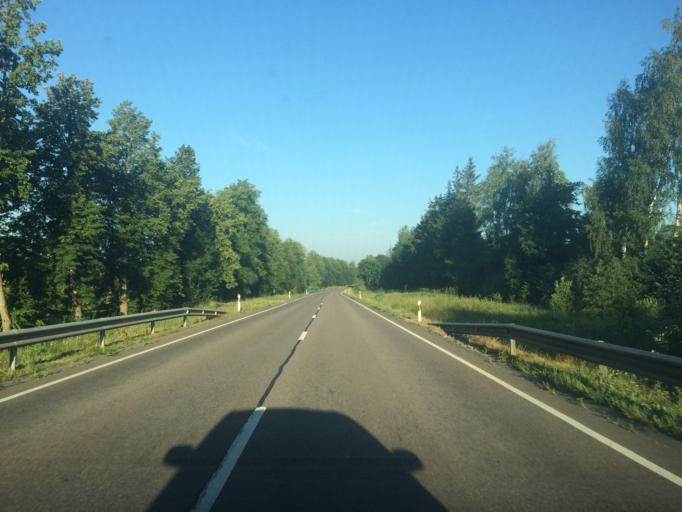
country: LT
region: Utenos apskritis
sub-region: Anyksciai
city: Anyksciai
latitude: 55.4024
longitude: 25.1814
